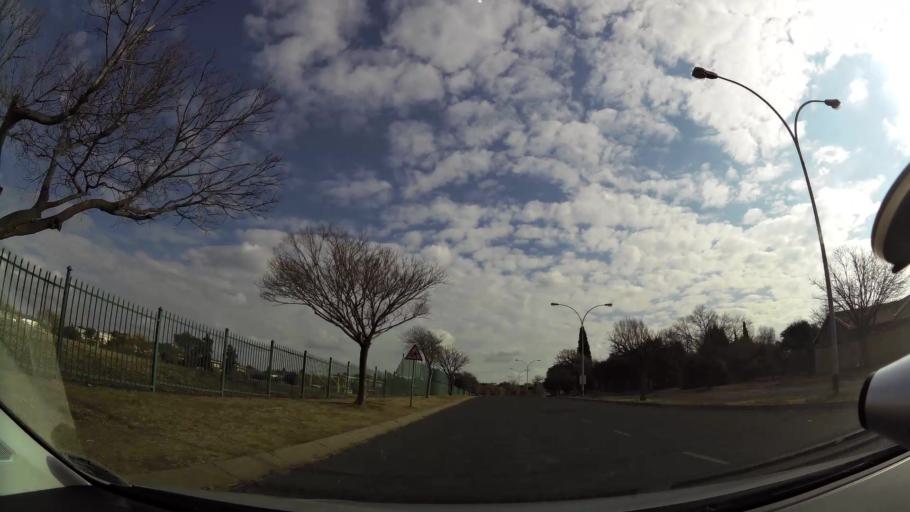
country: ZA
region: Orange Free State
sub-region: Mangaung Metropolitan Municipality
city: Bloemfontein
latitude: -29.0747
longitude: 26.2347
